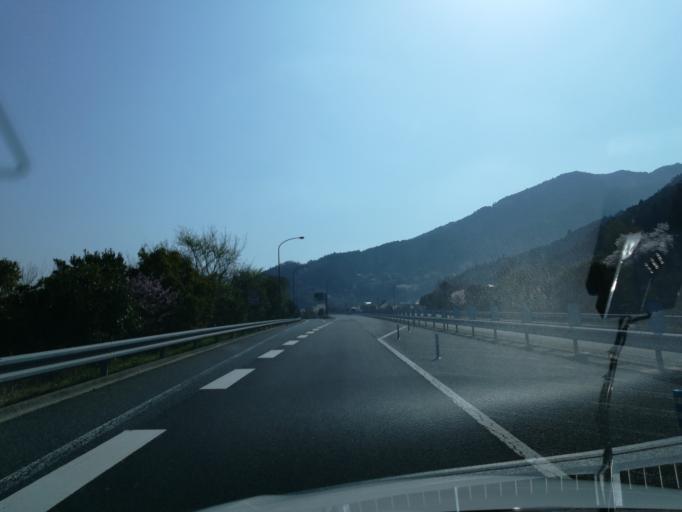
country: JP
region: Tokushima
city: Ikedacho
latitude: 34.0289
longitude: 133.8365
